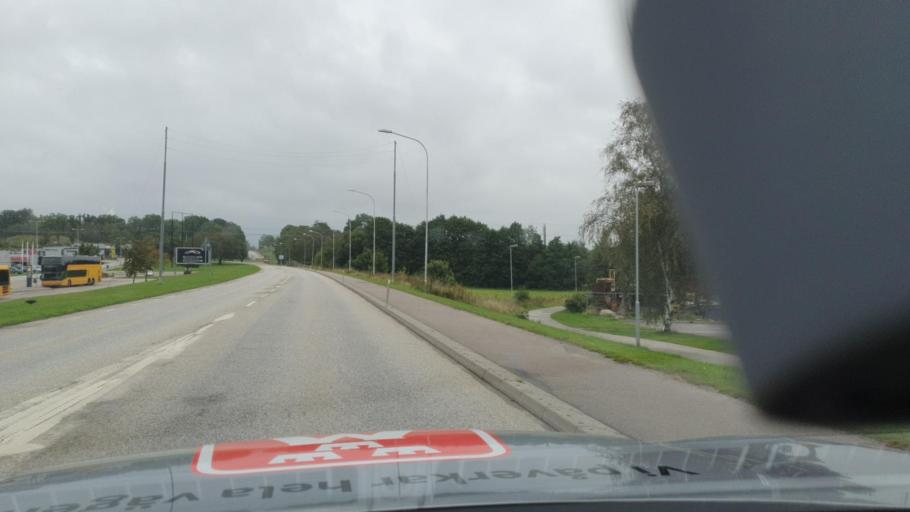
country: SE
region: Skane
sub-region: Horby Kommun
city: Hoerby
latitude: 55.8548
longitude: 13.6704
